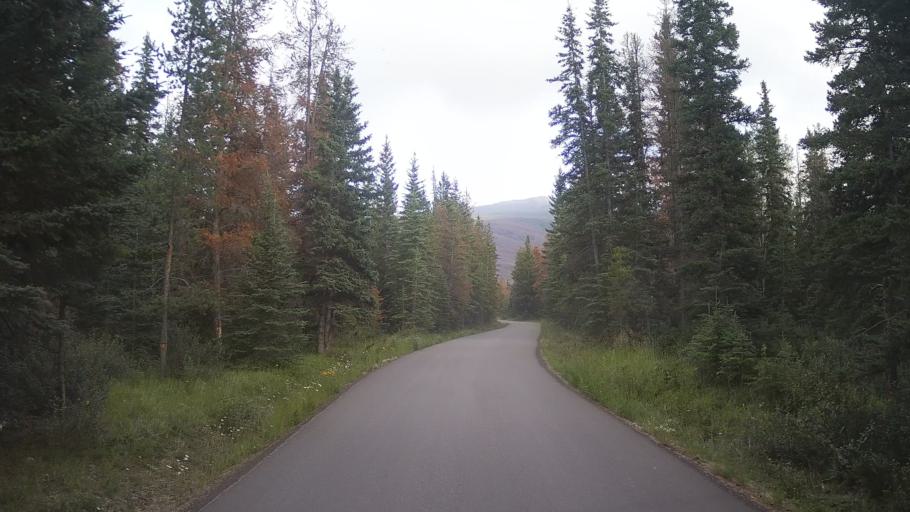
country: CA
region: Alberta
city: Jasper Park Lodge
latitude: 52.9312
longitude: -118.0322
